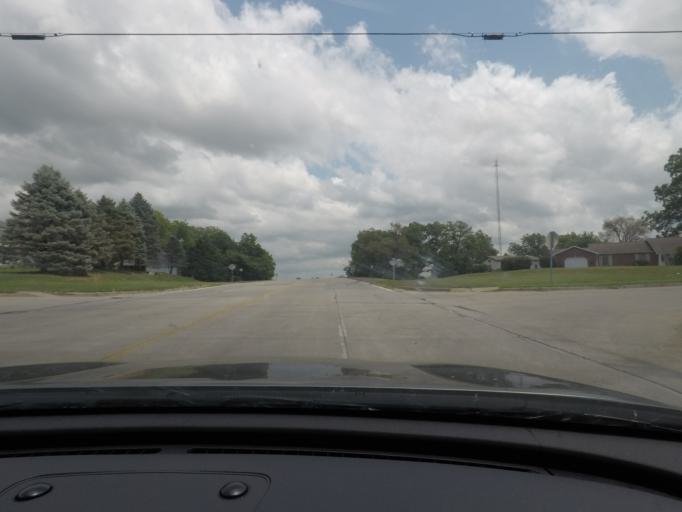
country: US
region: Missouri
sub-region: Carroll County
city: Carrollton
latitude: 39.3586
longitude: -93.4863
